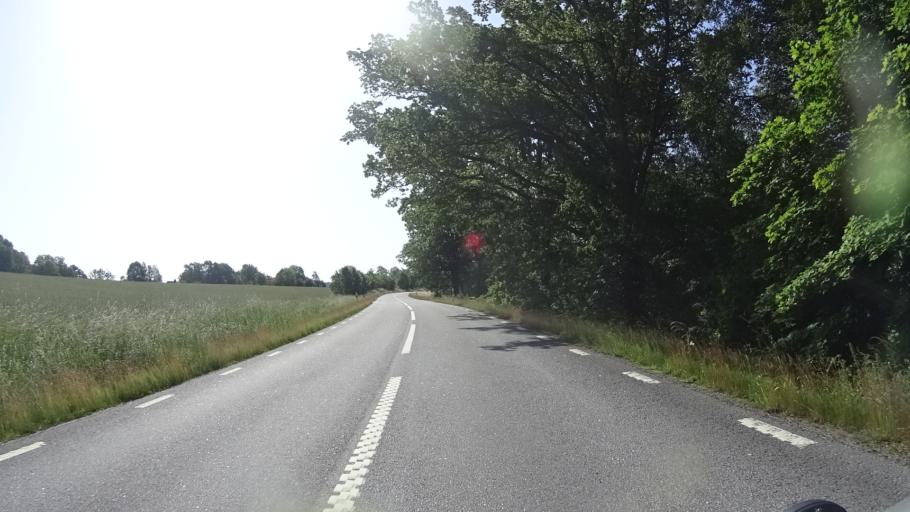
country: SE
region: OEstergoetland
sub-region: Atvidabergs Kommun
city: Atvidaberg
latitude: 58.1408
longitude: 16.0834
